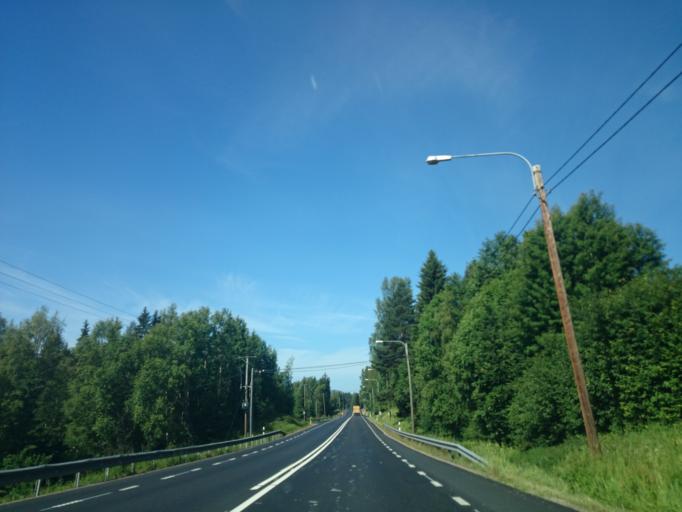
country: SE
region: Vaesternorrland
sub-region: Sundsvalls Kommun
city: Matfors
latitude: 62.4107
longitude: 16.6594
